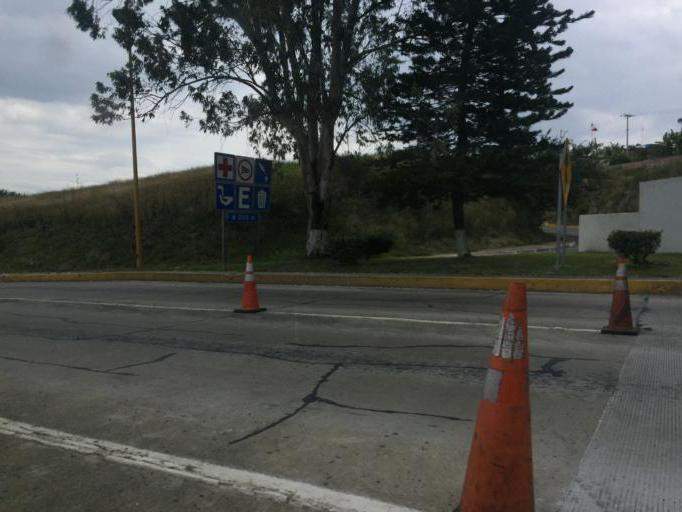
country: MX
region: Jalisco
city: Ocotlan
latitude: 20.4058
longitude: -102.7388
